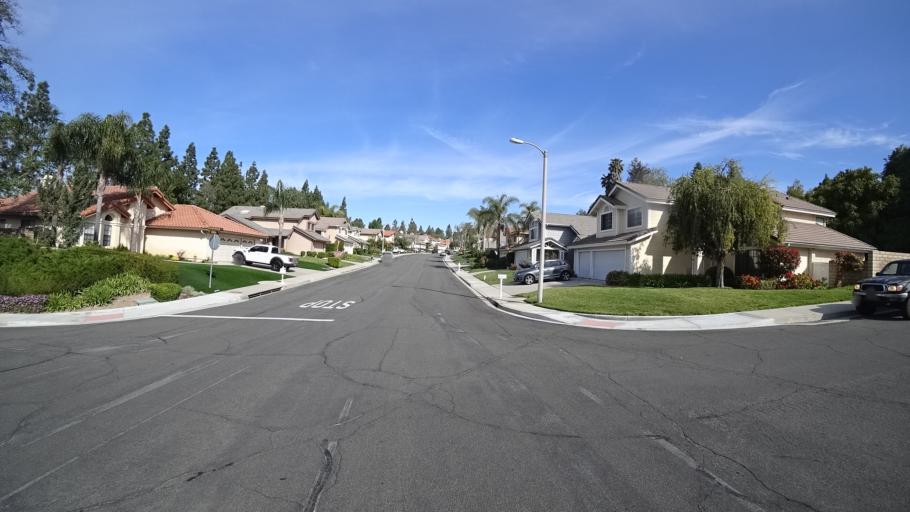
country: US
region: California
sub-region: Ventura County
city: Thousand Oaks
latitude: 34.2141
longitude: -118.8407
